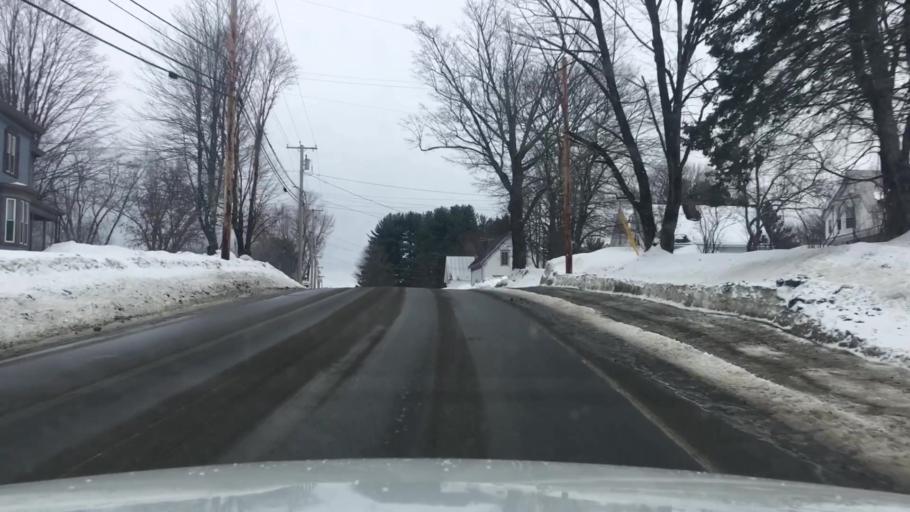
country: US
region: Maine
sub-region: Somerset County
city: Norridgewock
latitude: 44.7097
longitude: -69.7911
